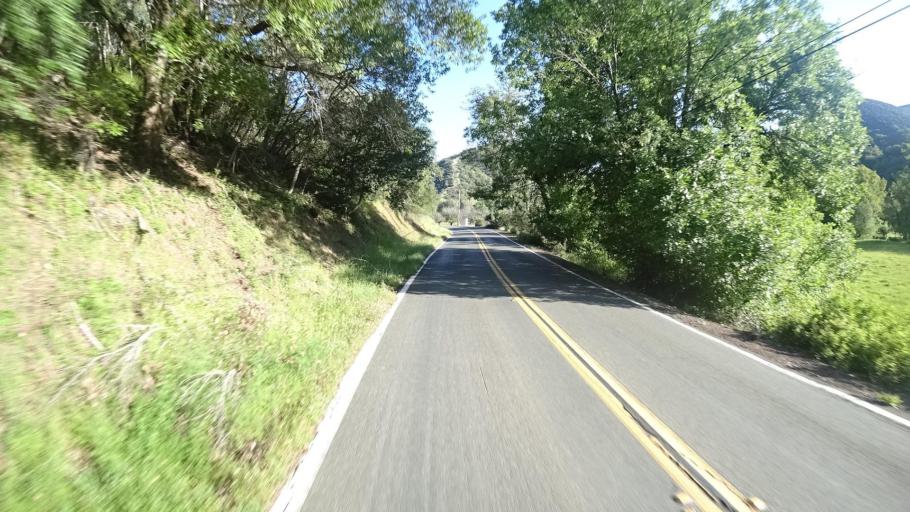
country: US
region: California
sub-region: Lake County
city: Upper Lake
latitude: 39.1392
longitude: -123.0009
